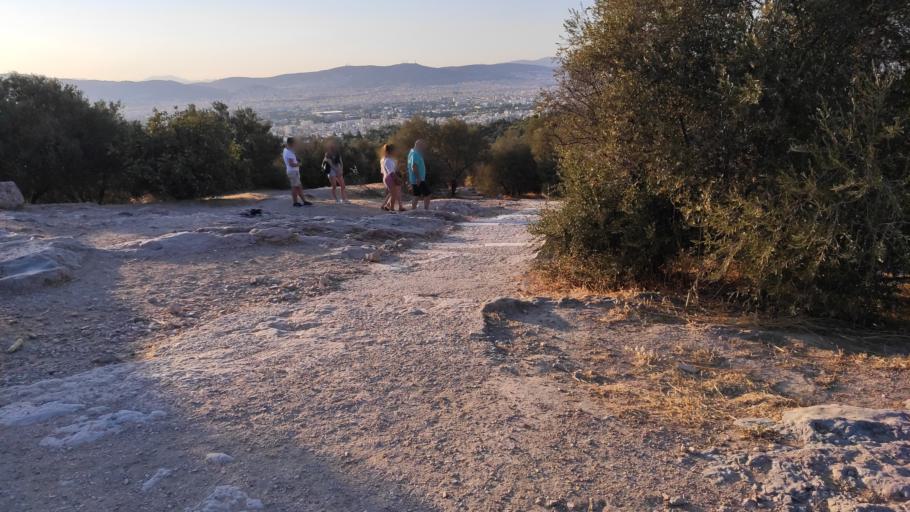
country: GR
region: Attica
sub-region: Nomarchia Athinas
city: Athens
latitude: 37.9678
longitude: 23.7210
